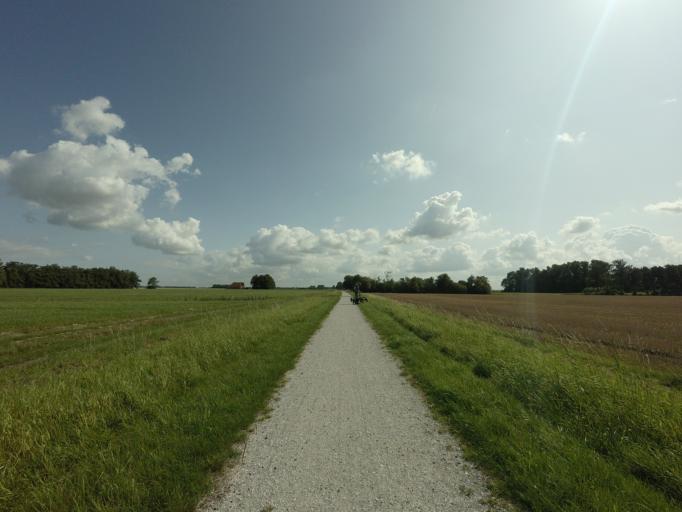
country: NL
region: Friesland
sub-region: Gemeente Het Bildt
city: Sint Annaparochie
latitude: 53.2801
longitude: 5.6719
